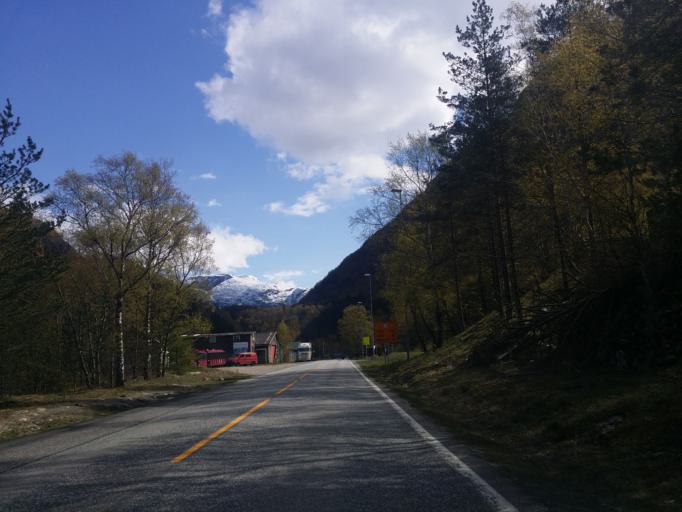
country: NO
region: Hordaland
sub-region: Eidfjord
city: Eidfjord
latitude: 60.4626
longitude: 7.0778
